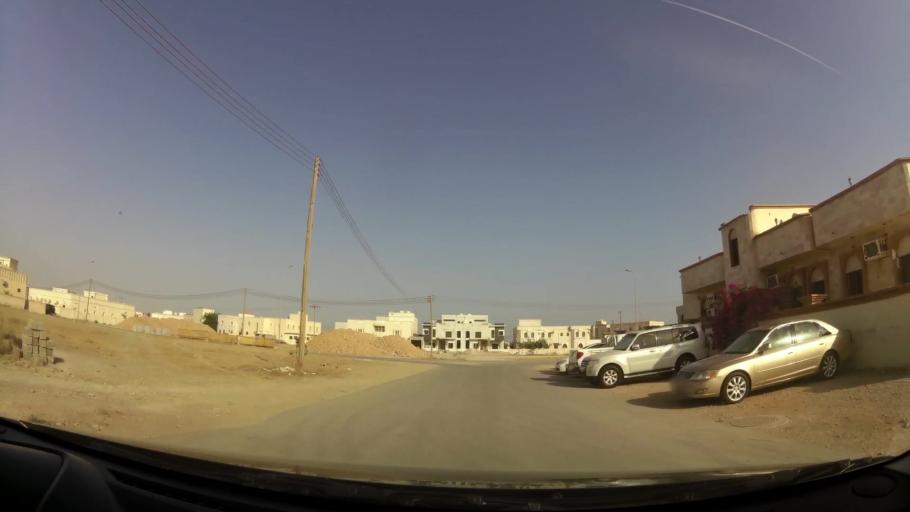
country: OM
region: Zufar
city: Salalah
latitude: 17.0225
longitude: 54.0209
